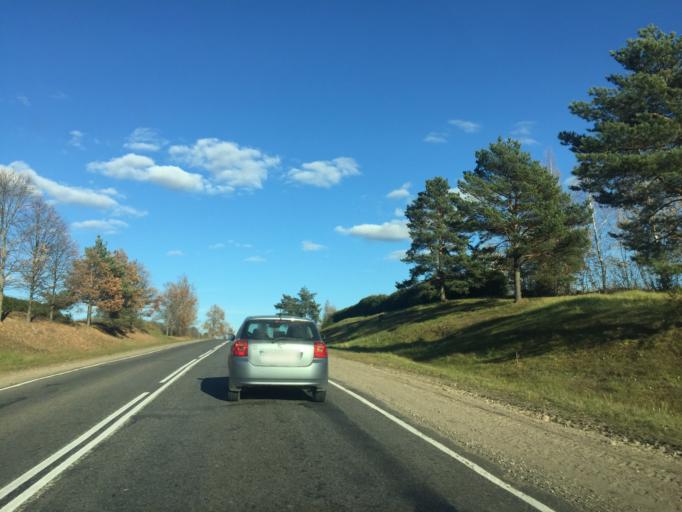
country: BY
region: Vitebsk
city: Dzisna
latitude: 55.2643
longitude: 28.1314
